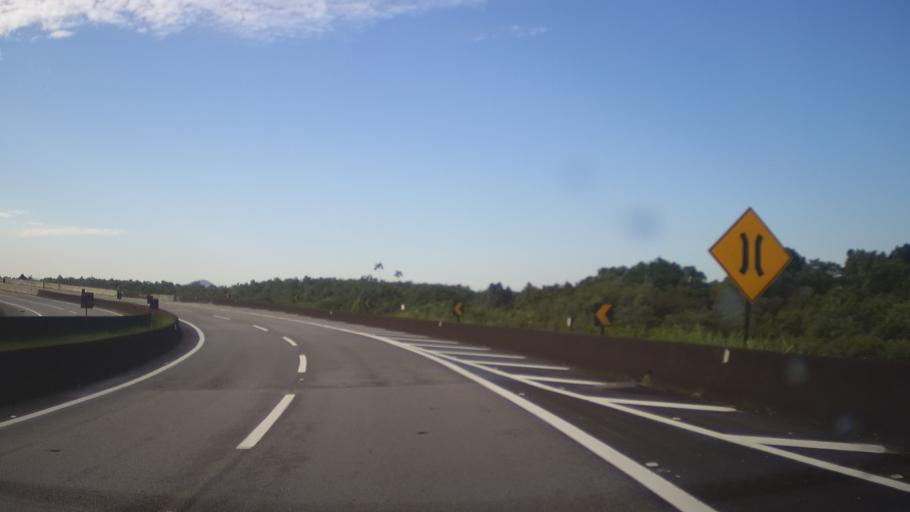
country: BR
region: Sao Paulo
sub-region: Cubatao
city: Cubatao
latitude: -23.9252
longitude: -46.4348
